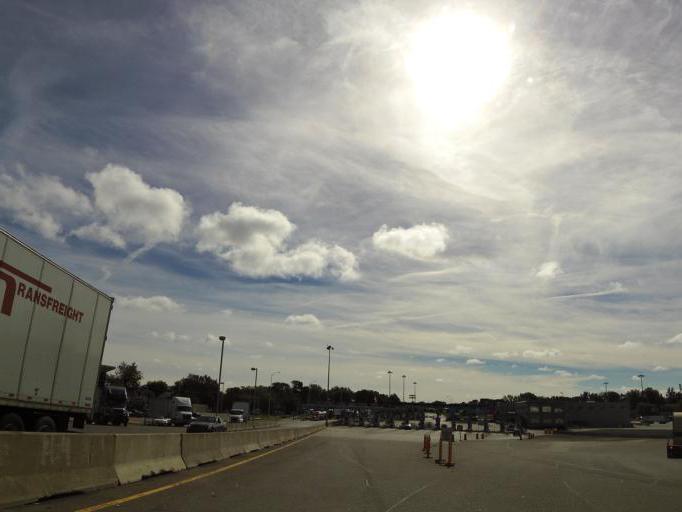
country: CA
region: Ontario
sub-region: Lambton County
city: Sarnia
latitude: 42.9946
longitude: -82.4132
